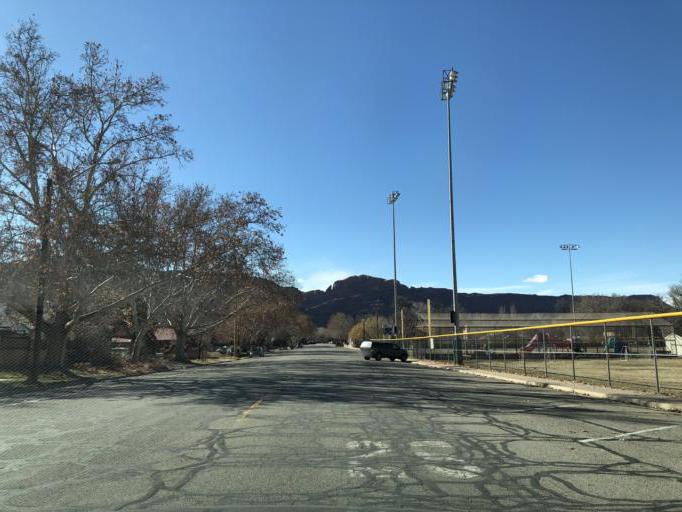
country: US
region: Utah
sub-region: Grand County
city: Moab
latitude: 38.5718
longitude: -109.5450
